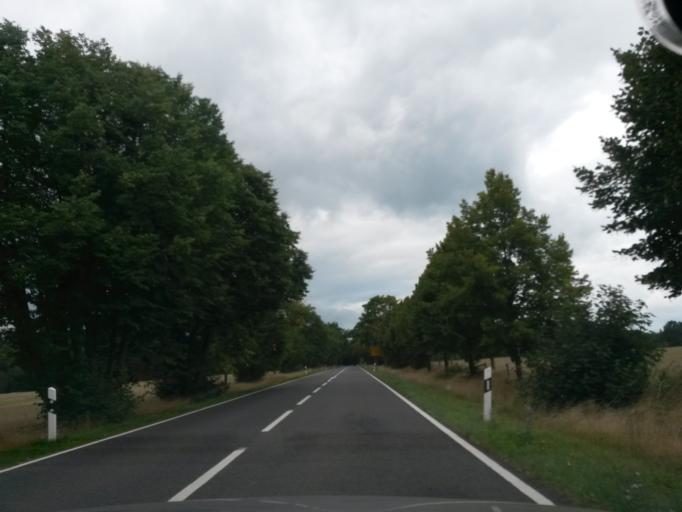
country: DE
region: Brandenburg
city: Gerswalde
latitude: 53.1401
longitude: 13.8685
